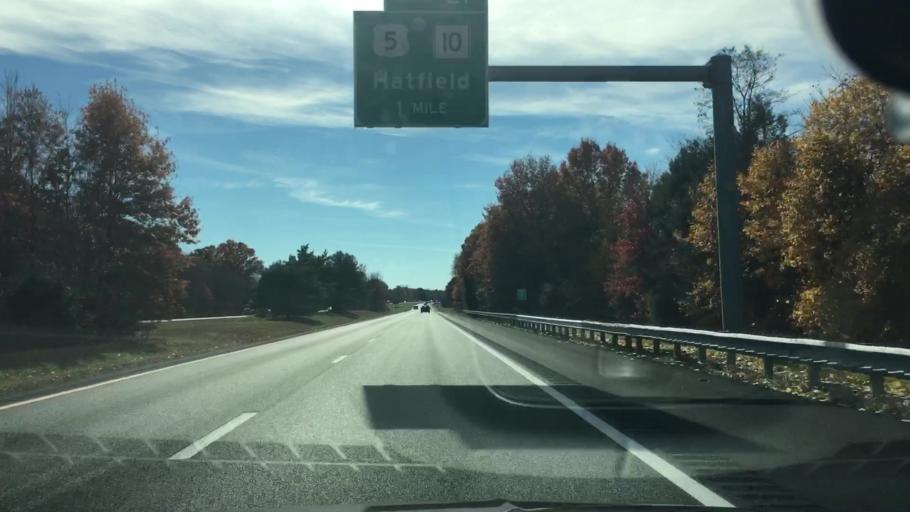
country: US
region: Massachusetts
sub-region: Hampshire County
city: Hatfield
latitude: 42.3768
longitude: -72.6326
